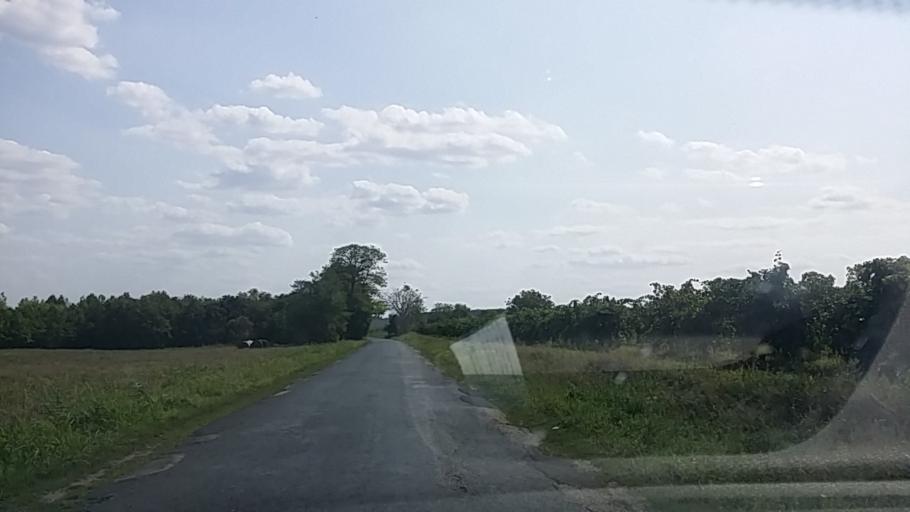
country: HU
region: Gyor-Moson-Sopron
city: Fertorakos
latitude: 47.6969
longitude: 16.6606
